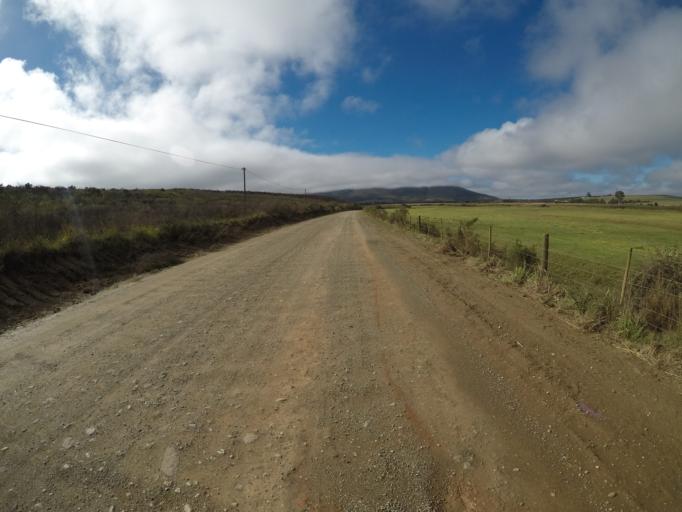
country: ZA
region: Western Cape
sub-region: Cape Winelands District Municipality
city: Ashton
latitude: -34.1238
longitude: 19.8283
